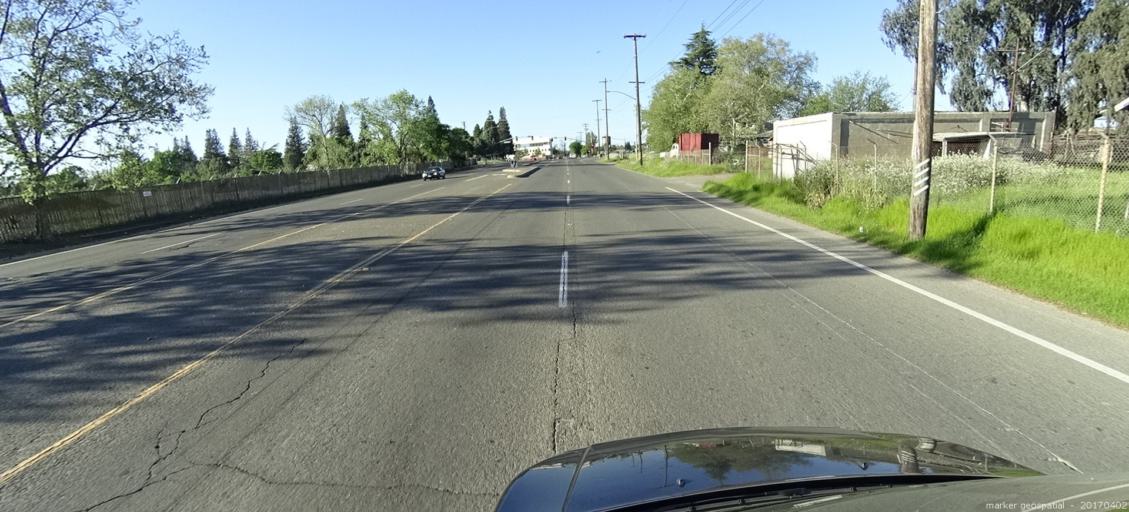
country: US
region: California
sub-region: Sacramento County
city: Rosemont
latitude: 38.5428
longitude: -121.3908
